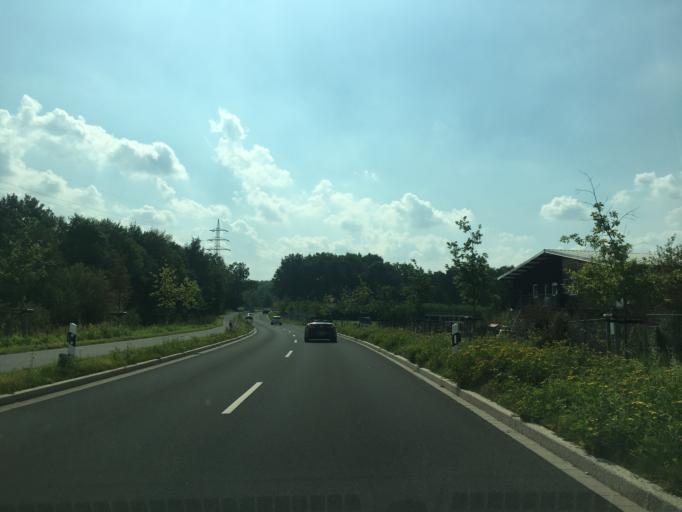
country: DE
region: North Rhine-Westphalia
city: Selm
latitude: 51.6931
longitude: 7.4872
